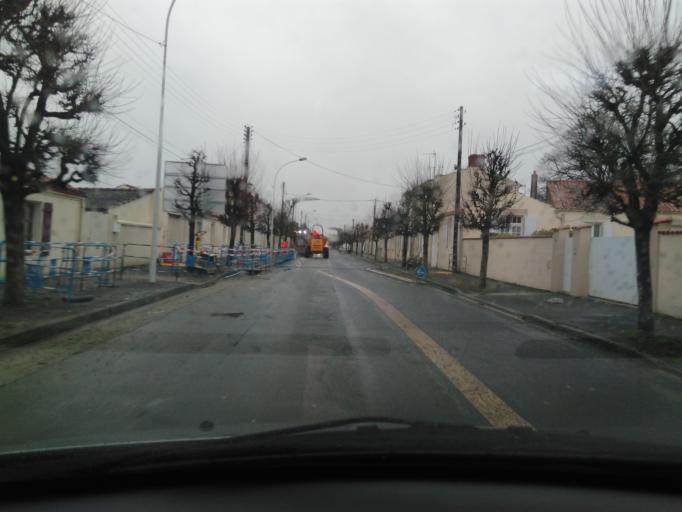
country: FR
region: Pays de la Loire
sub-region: Departement de la Vendee
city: Lucon
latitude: 46.4630
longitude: -1.1712
